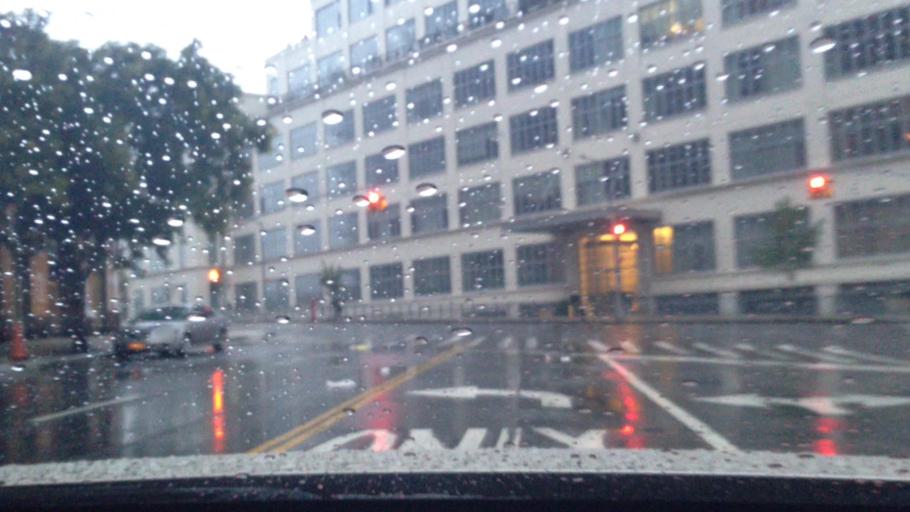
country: US
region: New York
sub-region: Queens County
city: Long Island City
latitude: 40.7466
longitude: -73.9420
